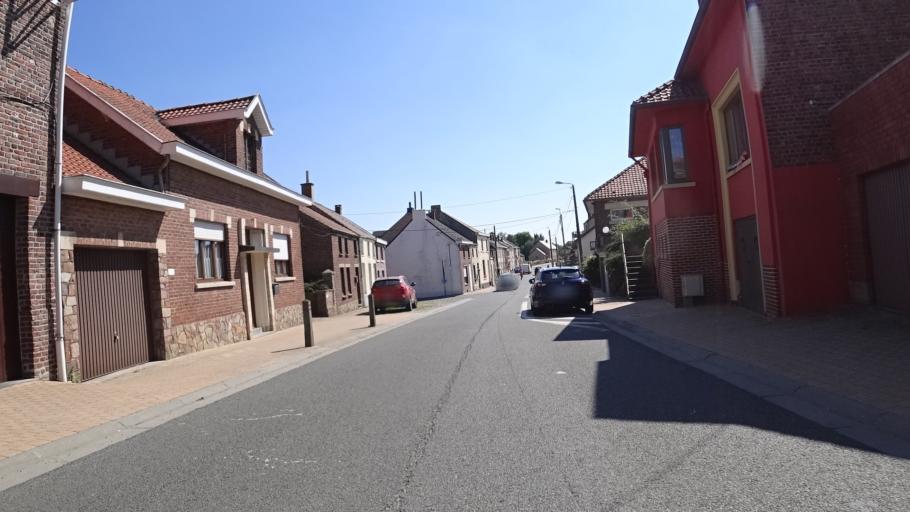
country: BE
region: Wallonia
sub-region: Province du Brabant Wallon
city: Jodoigne
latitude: 50.7225
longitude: 4.8627
